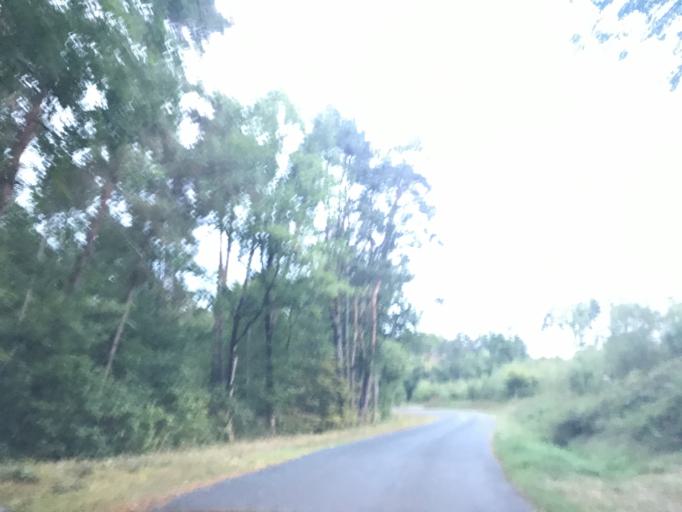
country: FR
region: Auvergne
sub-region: Departement du Puy-de-Dome
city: Escoutoux
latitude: 45.7935
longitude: 3.5663
